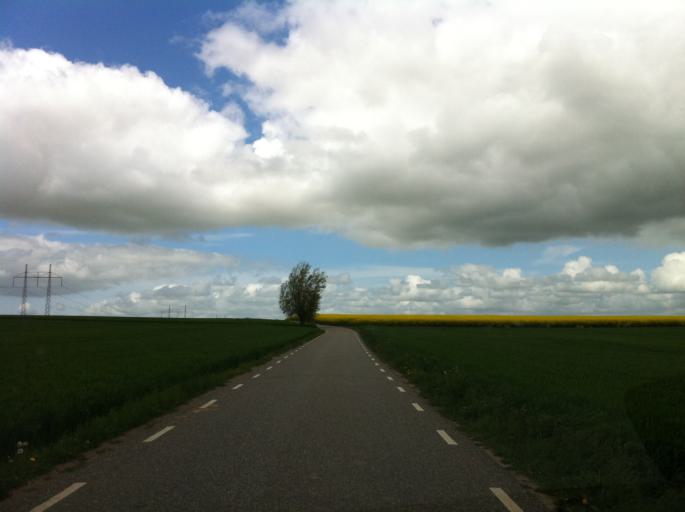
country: SE
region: Skane
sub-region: Svalovs Kommun
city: Teckomatorp
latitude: 55.8494
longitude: 13.0668
